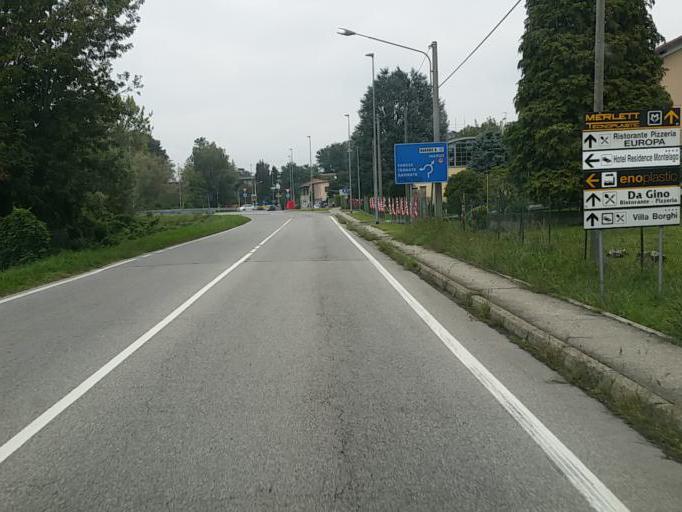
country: IT
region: Lombardy
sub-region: Provincia di Varese
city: Varano Borghi
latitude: 45.7661
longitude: 8.7033
